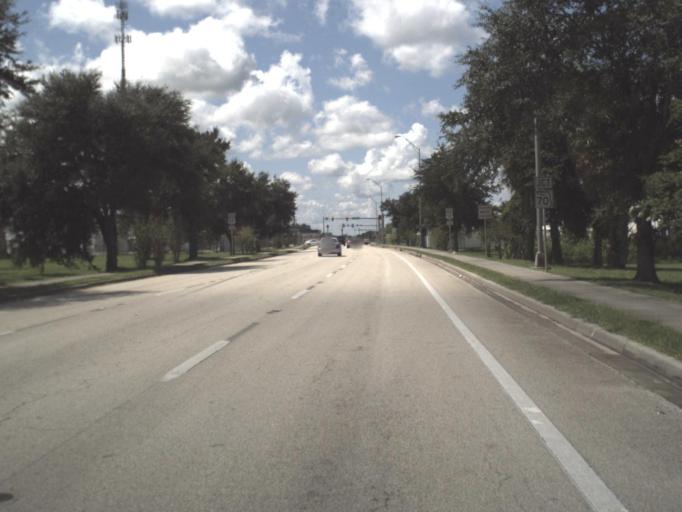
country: US
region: Florida
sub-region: DeSoto County
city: Arcadia
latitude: 27.2183
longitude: -81.8590
